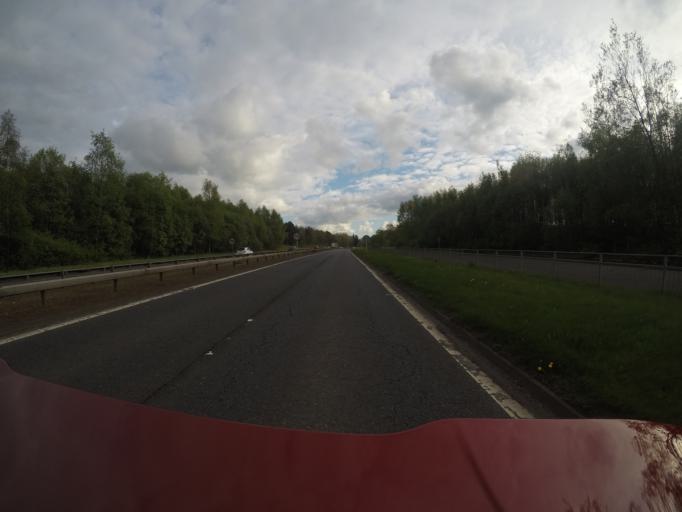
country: GB
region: Scotland
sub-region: West Dunbartonshire
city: Old Kilpatrick
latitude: 55.9097
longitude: -4.4729
